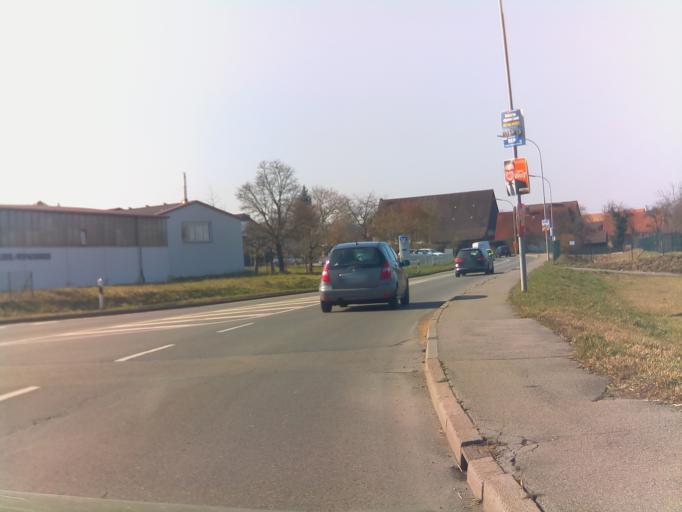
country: DE
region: Baden-Wuerttemberg
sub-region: Karlsruhe Region
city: Horb am Neckar
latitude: 48.4651
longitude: 8.7153
